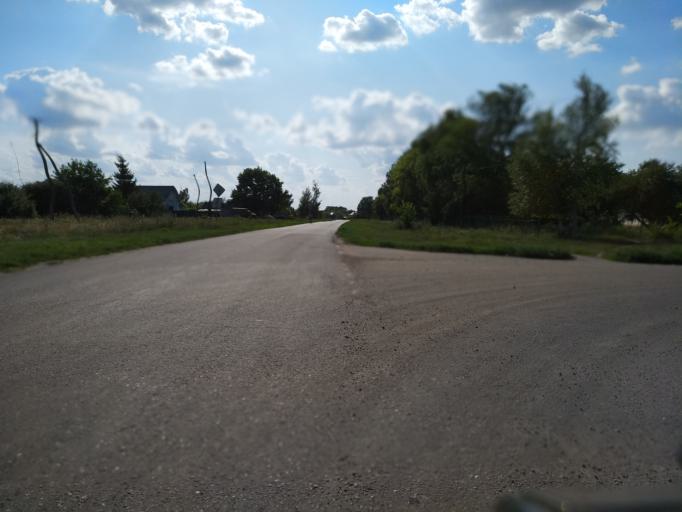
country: RU
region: Lipetsk
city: Dobrinka
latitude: 52.0389
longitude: 40.5397
